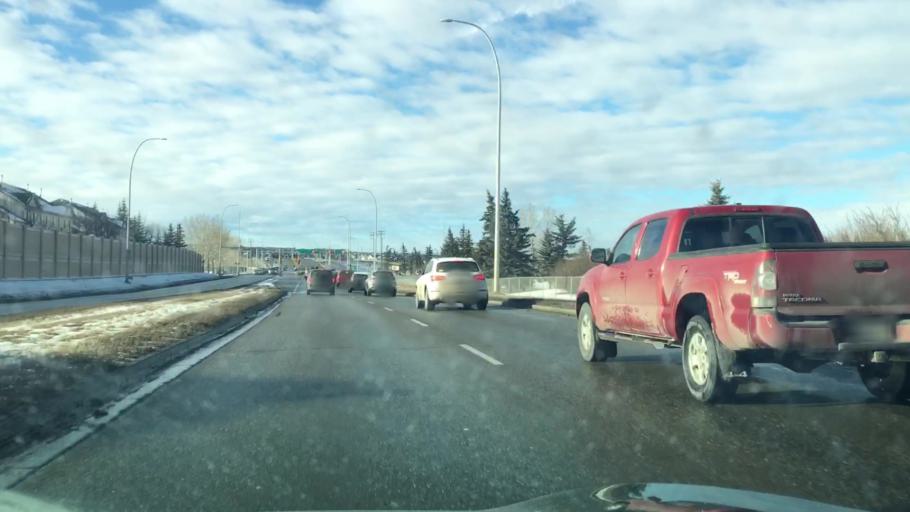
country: CA
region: Alberta
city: Calgary
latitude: 51.1521
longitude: -114.1041
